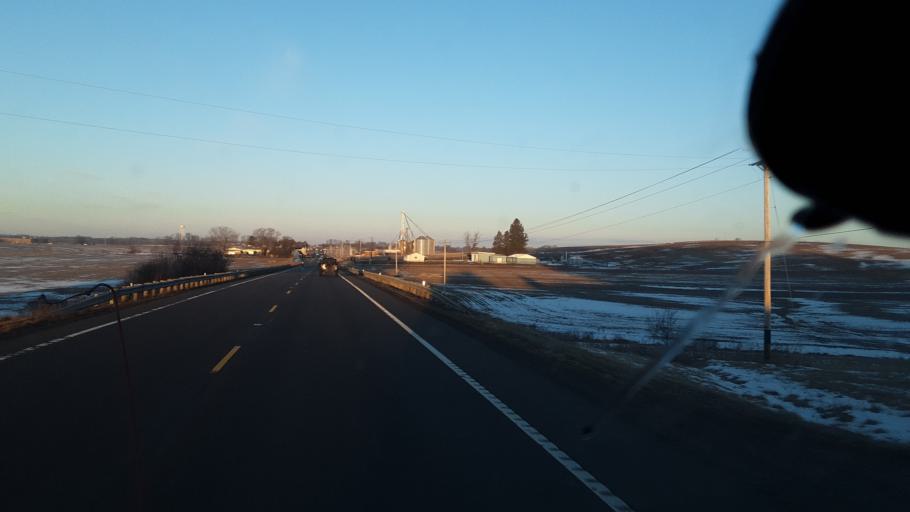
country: US
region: Ohio
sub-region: Perry County
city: Somerset
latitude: 39.8312
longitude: -82.3616
